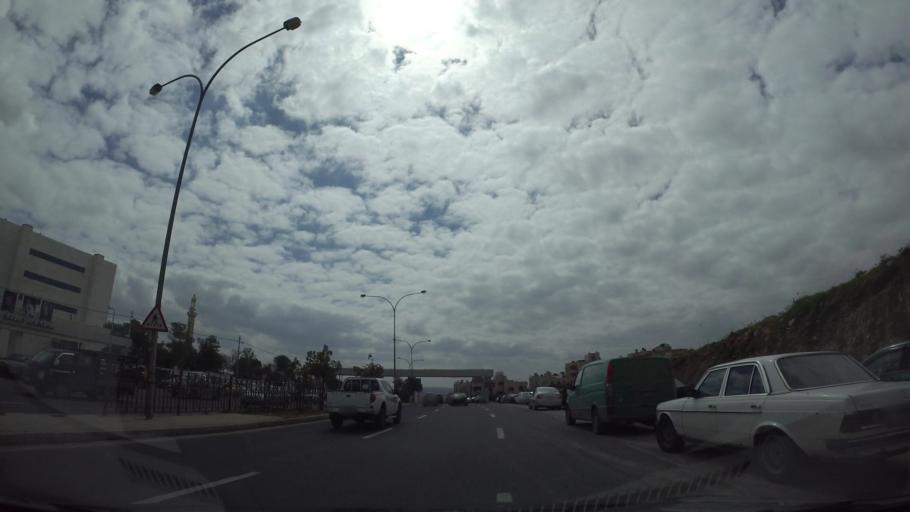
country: JO
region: Amman
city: Amman
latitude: 32.0011
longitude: 35.9177
